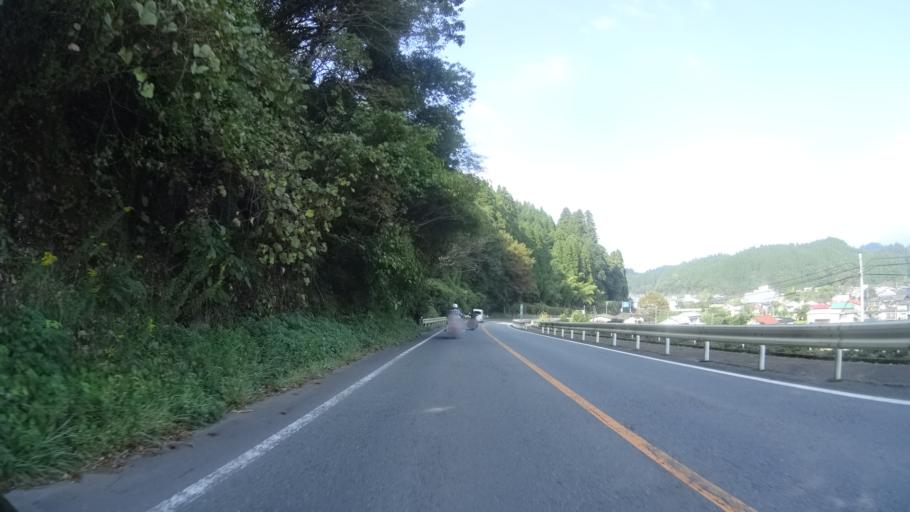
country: JP
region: Kumamoto
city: Aso
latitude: 33.0942
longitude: 131.0662
